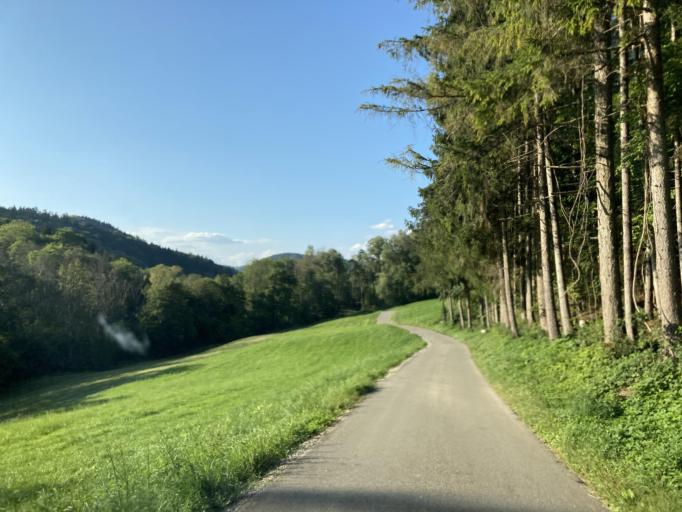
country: DE
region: Baden-Wuerttemberg
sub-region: Freiburg Region
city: Blumberg
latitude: 47.8229
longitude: 8.5107
